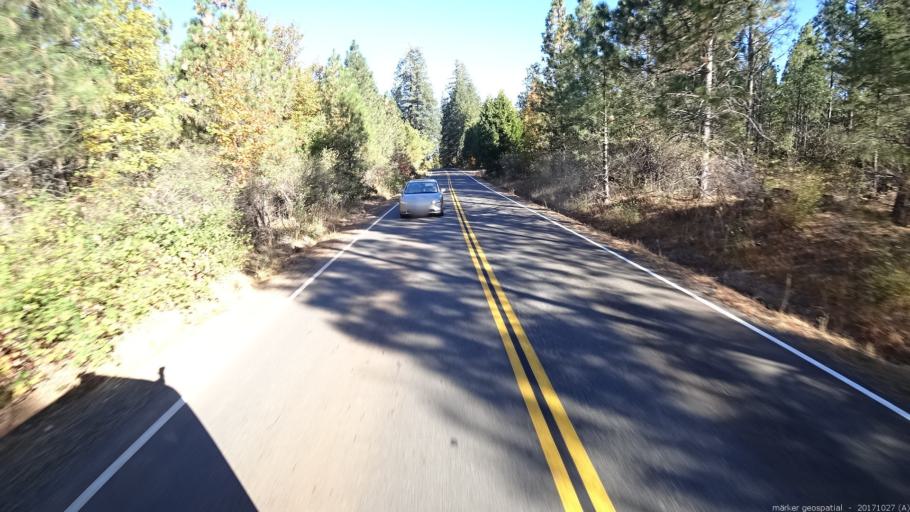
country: US
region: California
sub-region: Shasta County
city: Burney
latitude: 40.8847
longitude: -121.9084
